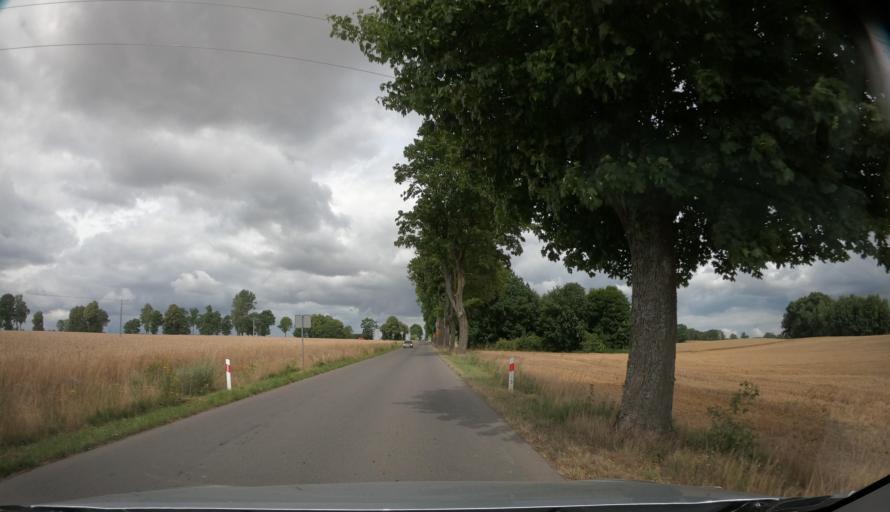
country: PL
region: West Pomeranian Voivodeship
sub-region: Koszalin
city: Koszalin
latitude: 54.1526
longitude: 16.0811
